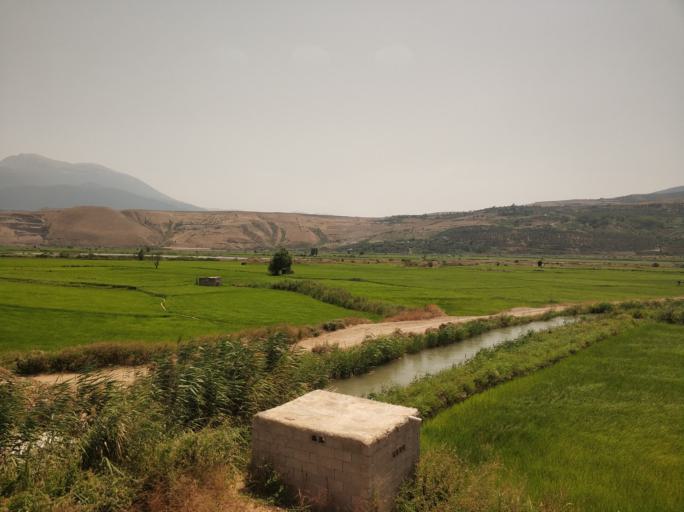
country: IR
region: Gilan
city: Pa'in-e Bazar-e Rudbar
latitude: 36.8814
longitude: 49.4979
